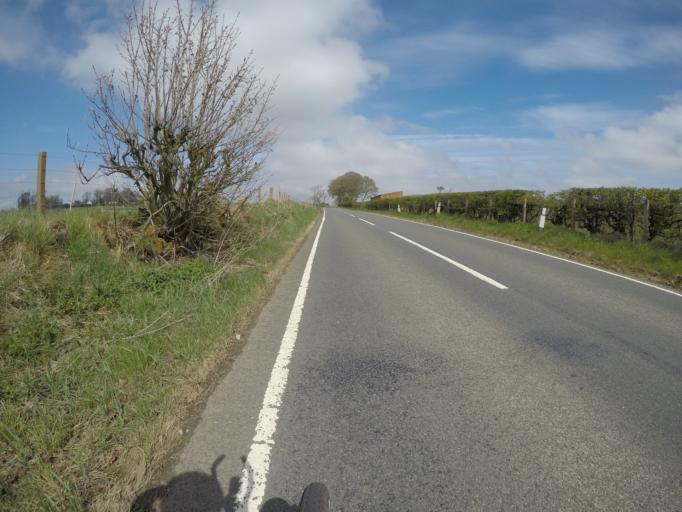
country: GB
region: Scotland
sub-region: East Ayrshire
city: Stewarton
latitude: 55.7064
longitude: -4.4623
